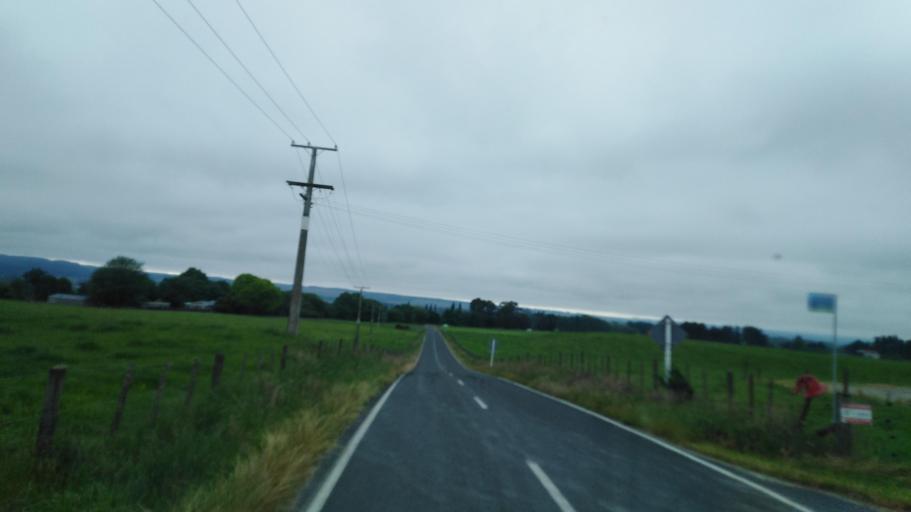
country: NZ
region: Bay of Plenty
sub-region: Rotorua District
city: Rotorua
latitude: -38.4050
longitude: 176.3293
